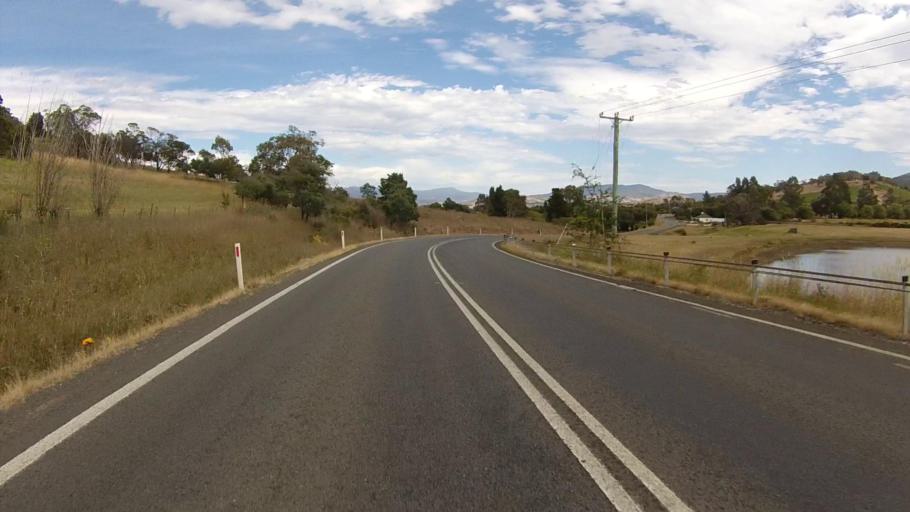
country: AU
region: Tasmania
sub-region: Brighton
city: Old Beach
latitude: -42.6917
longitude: 147.3359
